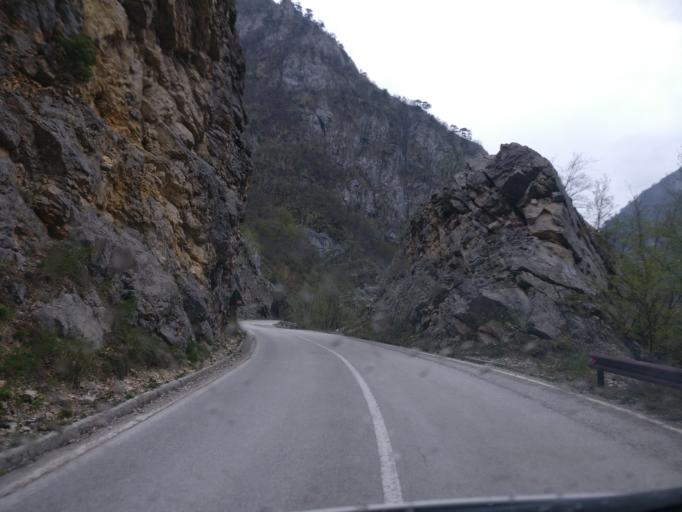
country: ME
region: Opstina Pluzine
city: Pluzine
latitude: 43.2301
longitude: 18.8457
